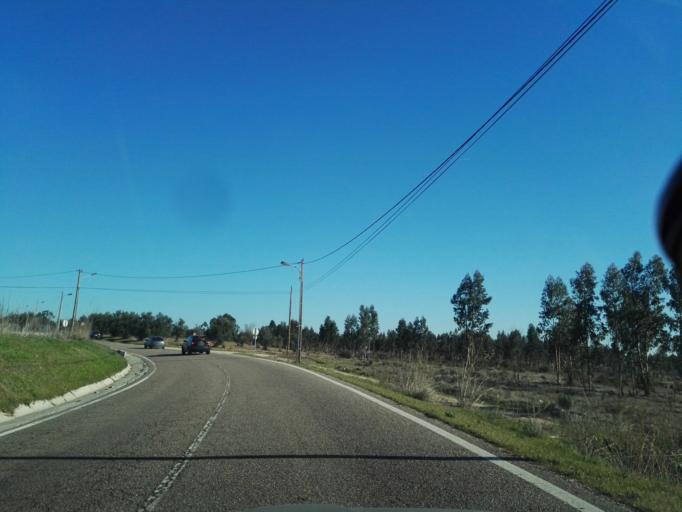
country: PT
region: Santarem
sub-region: Constancia
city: Constancia
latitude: 39.4807
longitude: -8.2965
